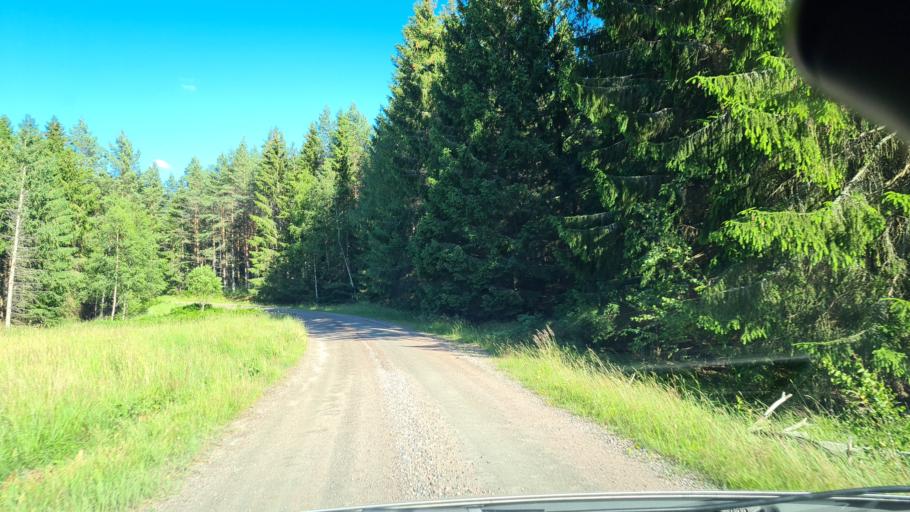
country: SE
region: Soedermanland
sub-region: Nykopings Kommun
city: Nykoping
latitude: 58.9083
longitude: 16.9300
